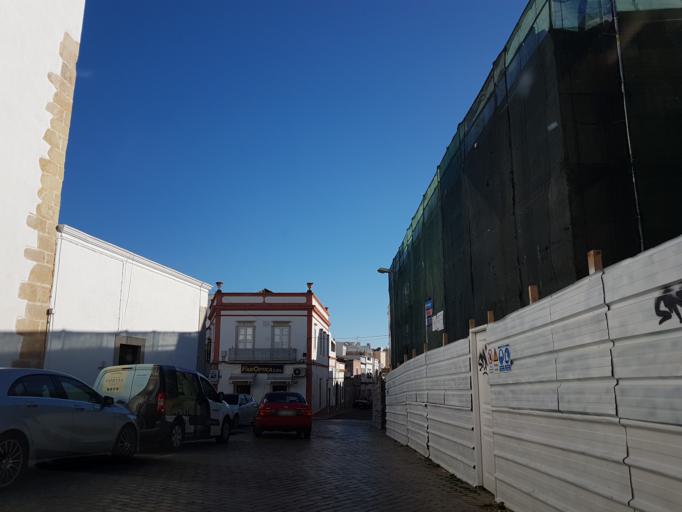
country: PT
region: Faro
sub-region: Faro
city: Faro
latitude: 37.0185
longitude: -7.9348
